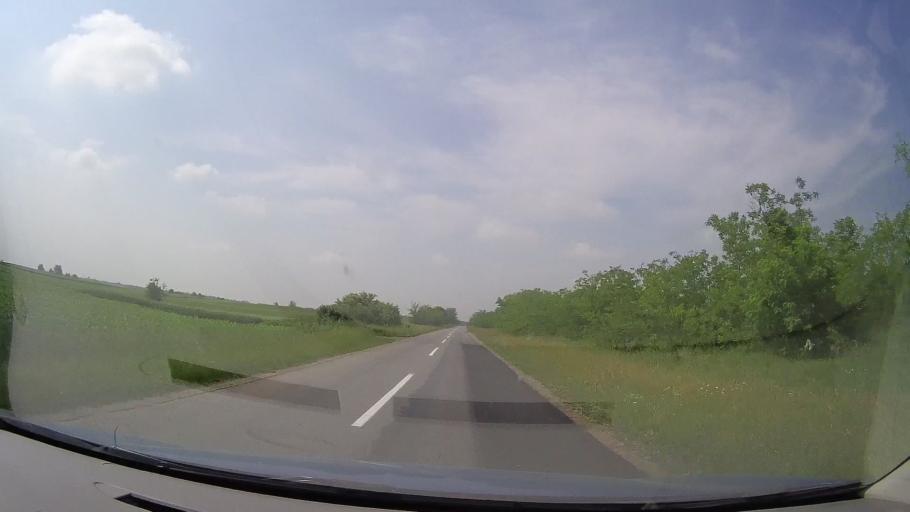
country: RS
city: Padina
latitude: 45.1408
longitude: 20.7395
